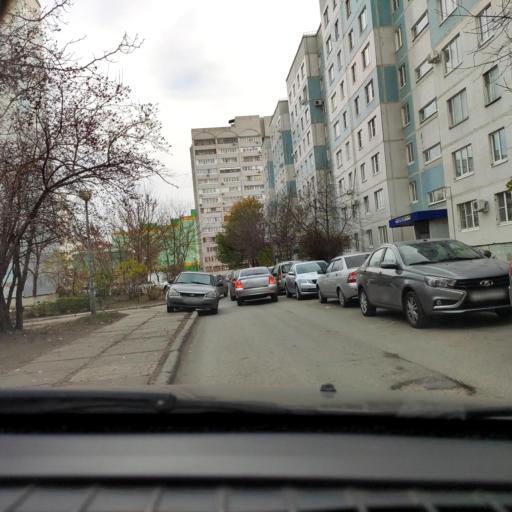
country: RU
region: Samara
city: Tol'yatti
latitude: 53.5443
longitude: 49.3565
